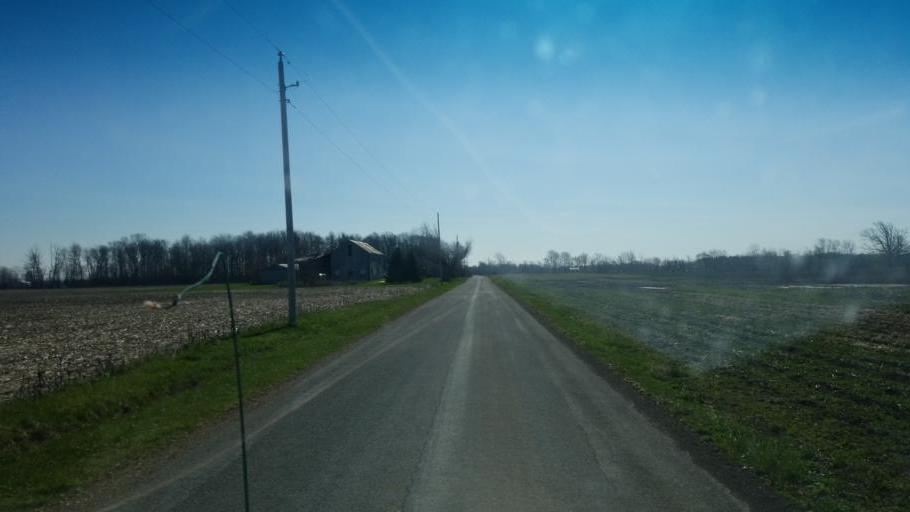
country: US
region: Ohio
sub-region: Hardin County
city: Forest
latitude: 40.7016
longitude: -83.5093
